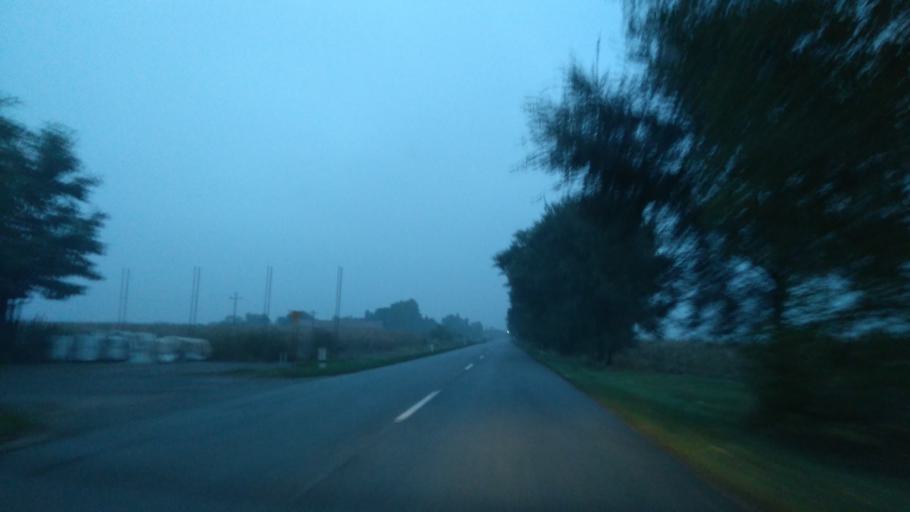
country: RS
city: Mol
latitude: 45.7477
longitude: 20.1241
